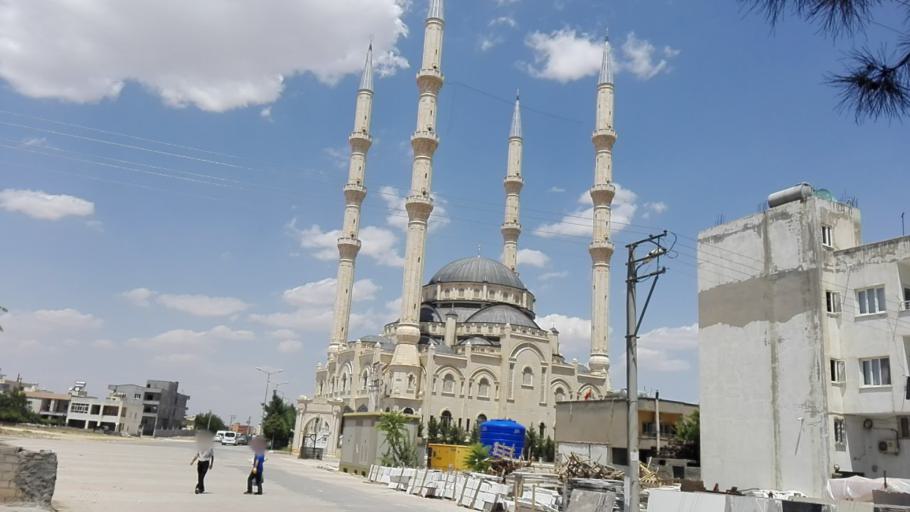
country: TR
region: Mardin
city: Midyat
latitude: 37.4181
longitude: 41.3607
